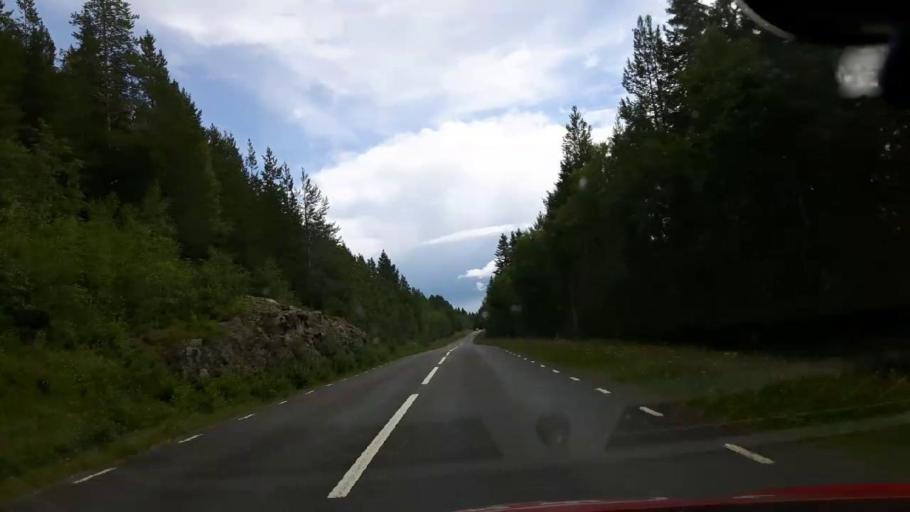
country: SE
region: Jaemtland
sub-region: Stroemsunds Kommun
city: Stroemsund
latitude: 64.3421
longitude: 14.9465
